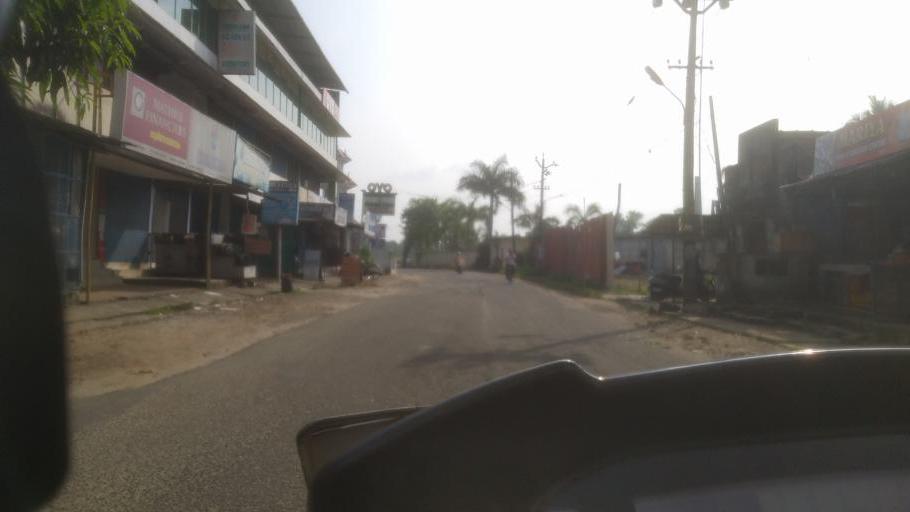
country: IN
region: Kerala
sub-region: Ernakulam
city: Angamali
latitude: 10.1616
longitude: 76.3818
